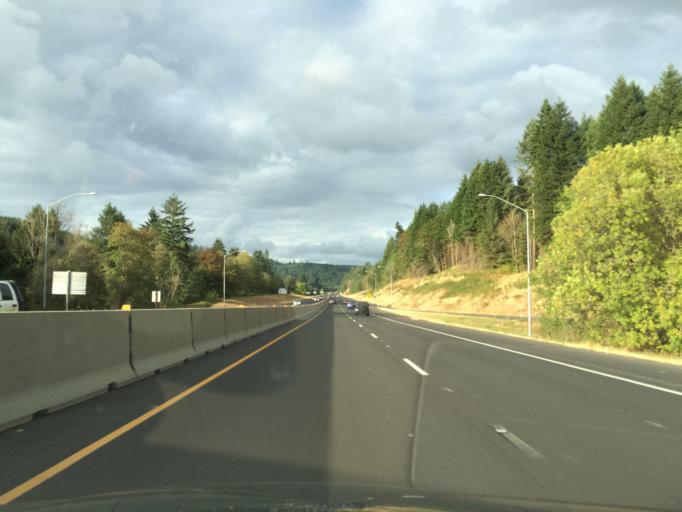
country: US
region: Oregon
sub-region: Douglas County
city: Drain
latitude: 43.7230
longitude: -123.2072
